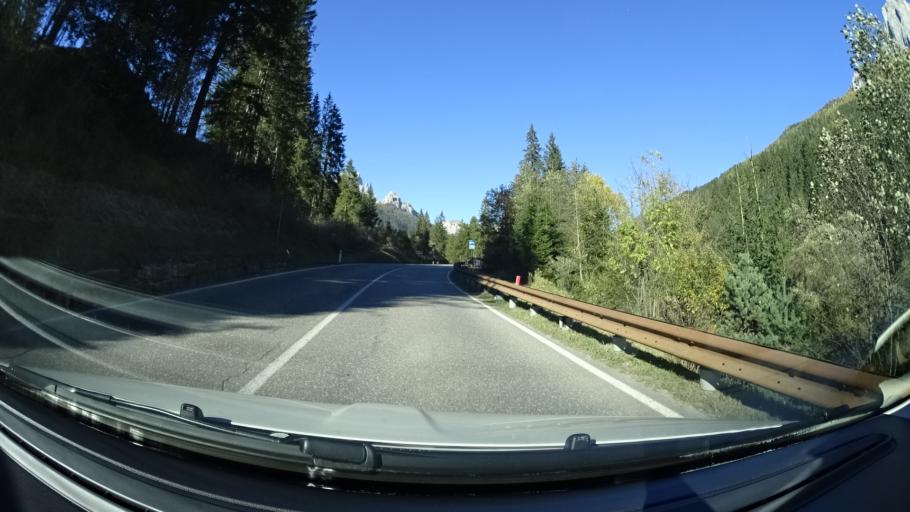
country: IT
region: Trentino-Alto Adige
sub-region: Provincia di Trento
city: Vigo di Fassa
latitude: 46.4067
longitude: 11.6766
